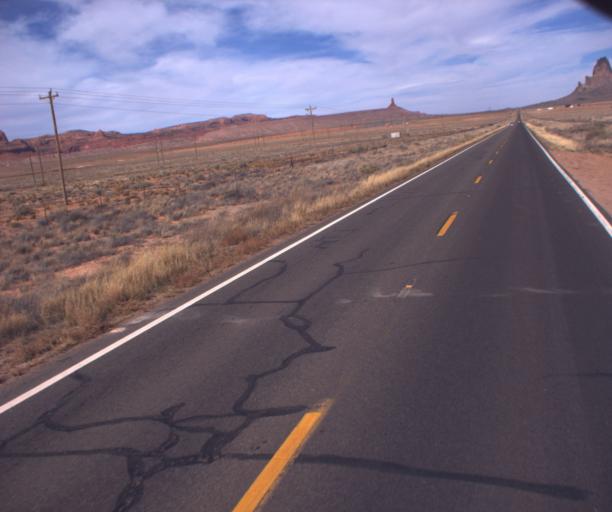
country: US
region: Arizona
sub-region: Navajo County
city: Kayenta
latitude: 36.7606
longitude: -110.2270
